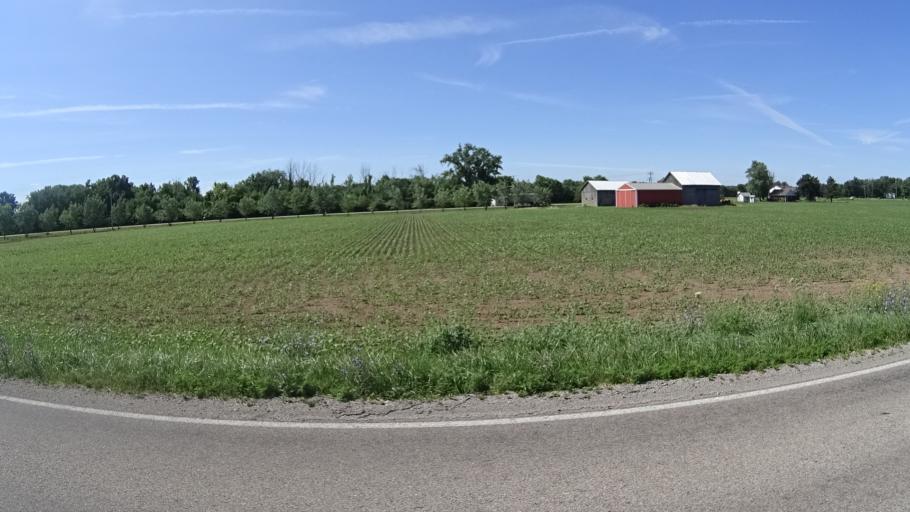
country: US
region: Ohio
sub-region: Ottawa County
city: Port Clinton
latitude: 41.4356
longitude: -82.8374
